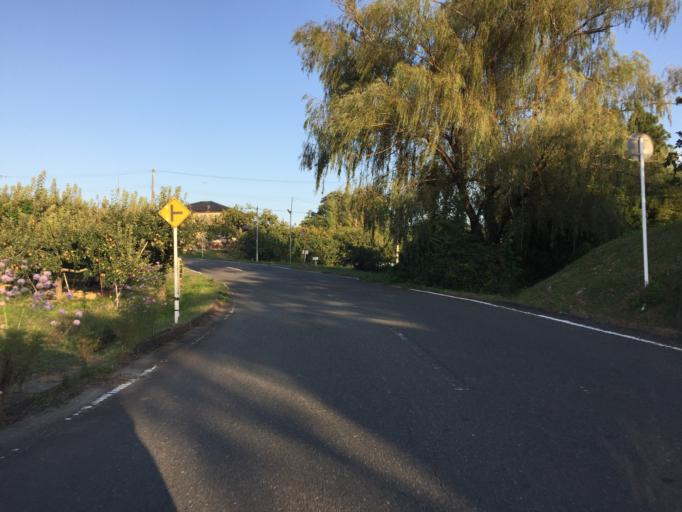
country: JP
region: Fukushima
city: Hobaramachi
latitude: 37.8034
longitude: 140.5683
